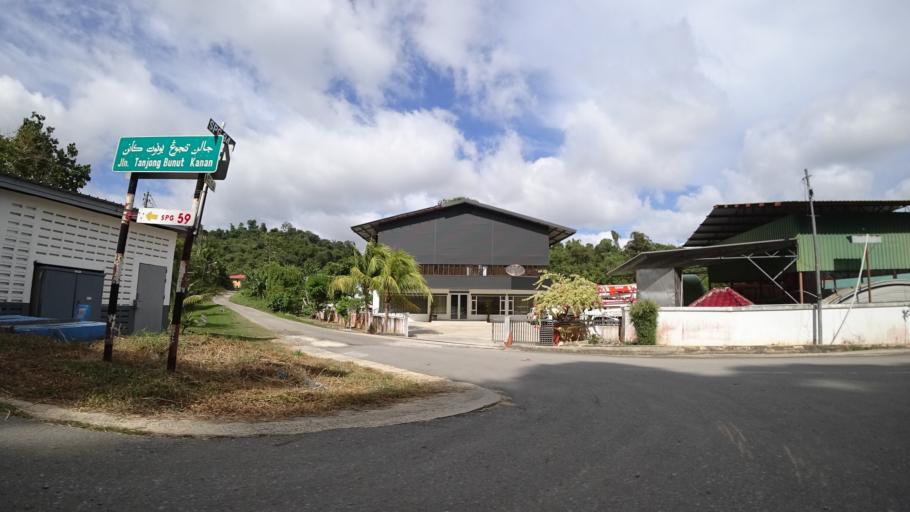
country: BN
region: Brunei and Muara
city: Bandar Seri Begawan
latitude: 4.8981
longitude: 114.8567
